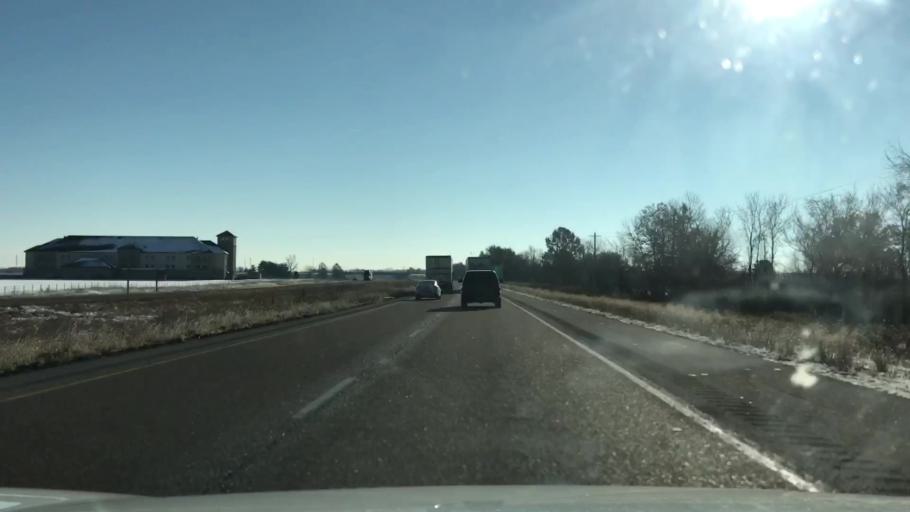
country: US
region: Illinois
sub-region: Saint Clair County
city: Scott Air Force Base
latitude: 38.5541
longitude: -89.8163
